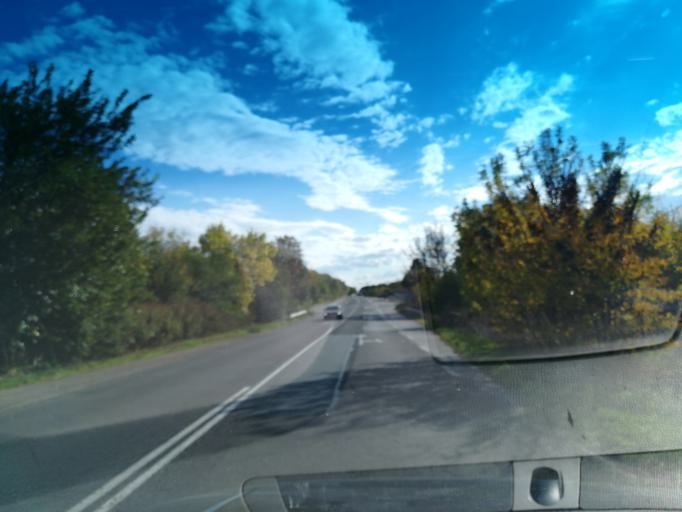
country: BG
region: Stara Zagora
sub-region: Obshtina Stara Zagora
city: Stara Zagora
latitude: 42.3617
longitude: 25.6556
